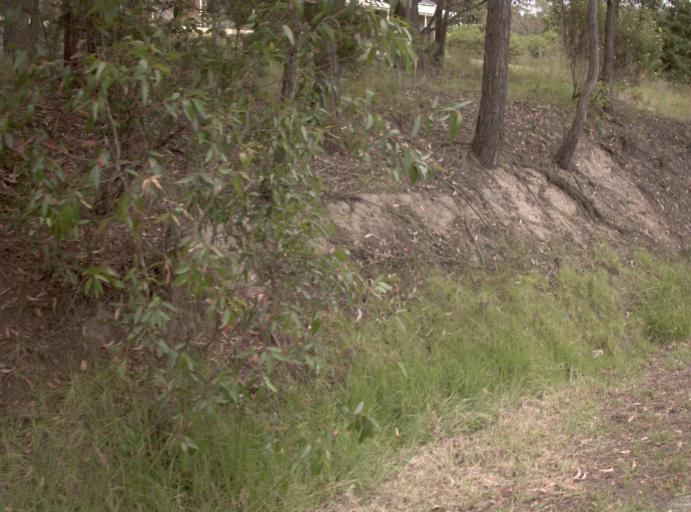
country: AU
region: Victoria
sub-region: Latrobe
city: Traralgon
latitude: -38.4921
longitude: 146.6422
